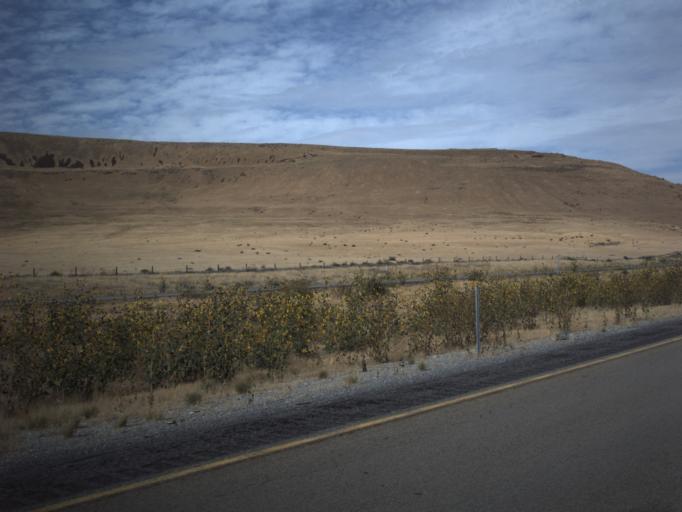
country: US
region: Utah
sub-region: Tooele County
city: Grantsville
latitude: 40.8130
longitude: -112.8728
